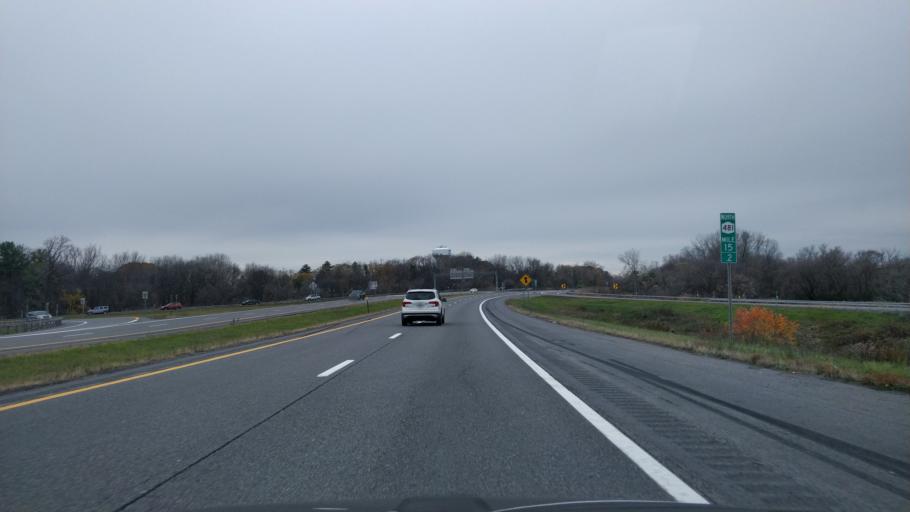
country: US
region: New York
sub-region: Onondaga County
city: North Syracuse
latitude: 43.1418
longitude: -76.1143
